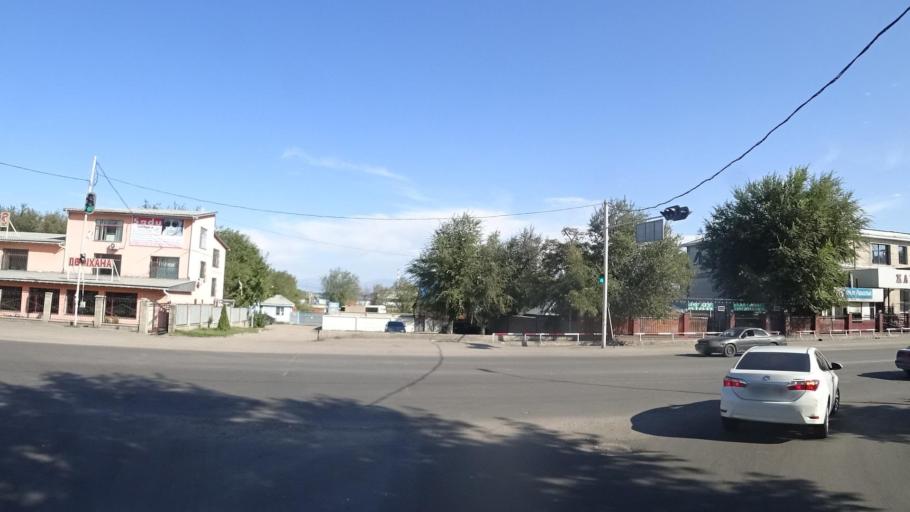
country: KZ
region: Almaty Oblysy
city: Energeticheskiy
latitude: 43.4254
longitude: 77.0242
